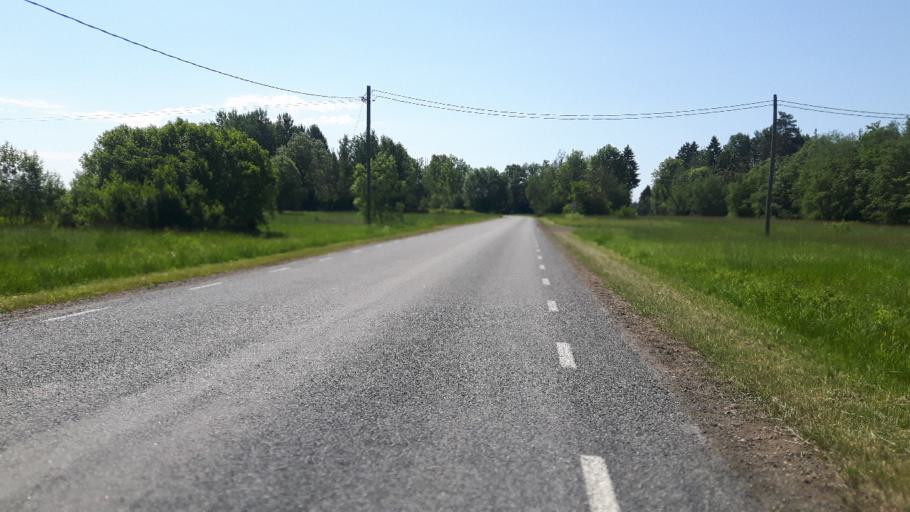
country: EE
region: Paernumaa
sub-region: Vaendra vald (alev)
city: Vandra
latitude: 58.6003
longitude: 25.0220
